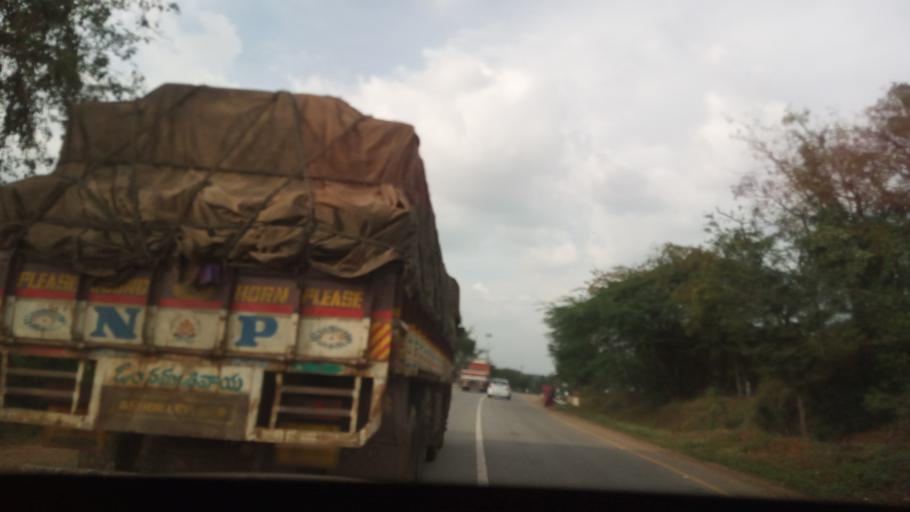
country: IN
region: Karnataka
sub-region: Tumkur
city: Kunigal
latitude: 12.8725
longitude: 77.0407
